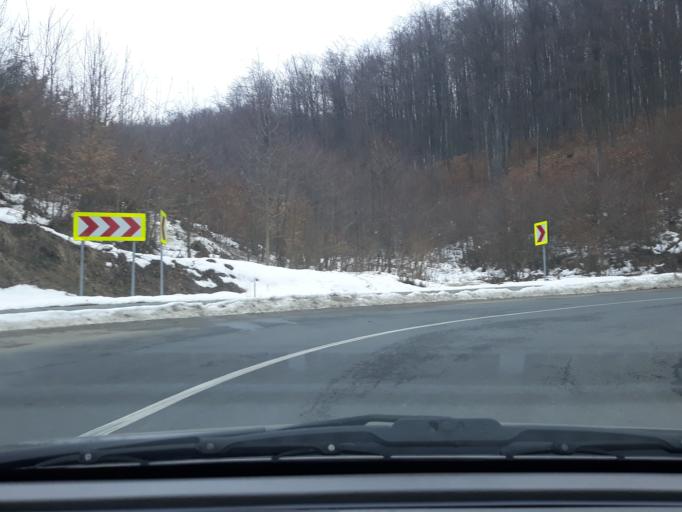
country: RO
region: Bihor
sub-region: Oras Alesd
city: Padurea Neagra
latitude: 47.1304
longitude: 22.4218
